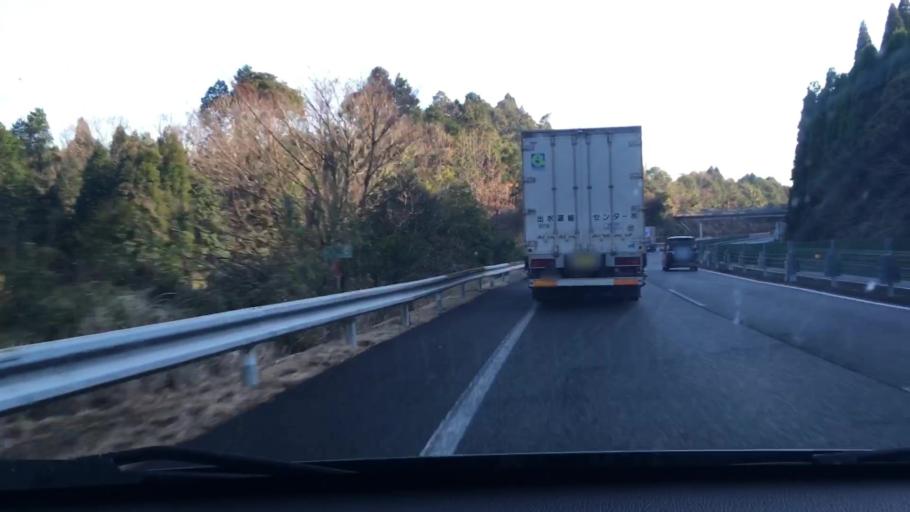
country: JP
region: Kagoshima
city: Kajiki
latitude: 31.8308
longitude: 130.6933
